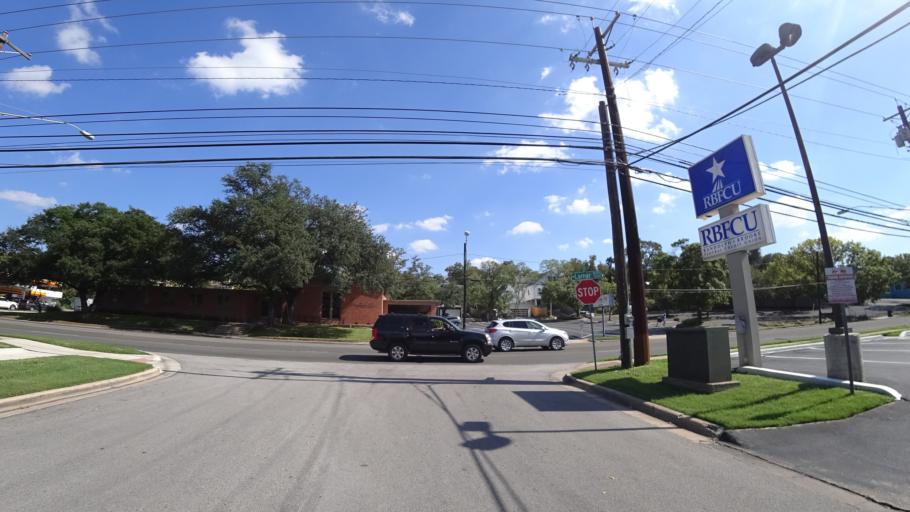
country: US
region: Texas
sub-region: Travis County
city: Austin
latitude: 30.3011
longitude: -97.7460
